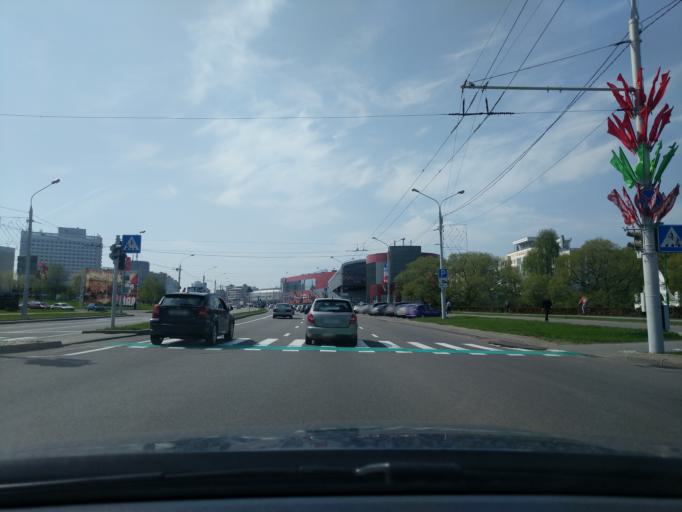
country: BY
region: Minsk
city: Novoye Medvezhino
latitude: 53.9368
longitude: 27.4939
